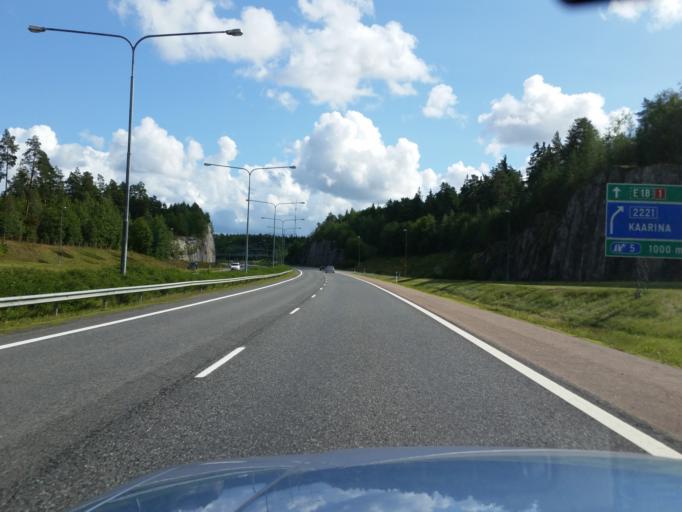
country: FI
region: Varsinais-Suomi
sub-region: Turku
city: Kaarina
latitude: 60.4284
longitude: 22.3279
